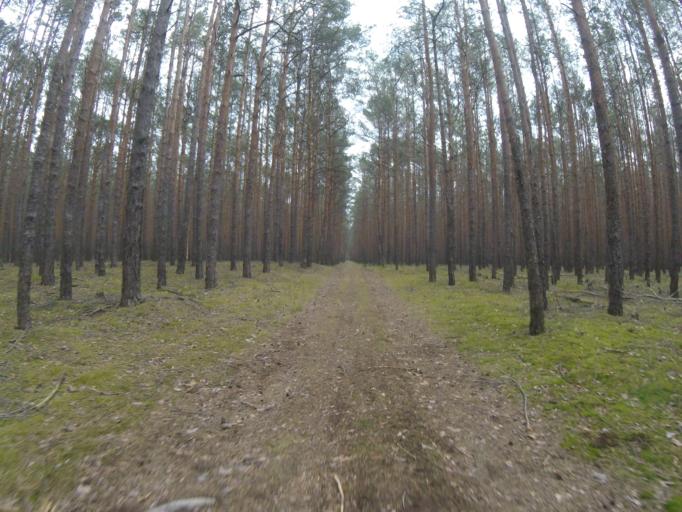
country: DE
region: Brandenburg
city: Halbe
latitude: 52.1085
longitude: 13.7120
